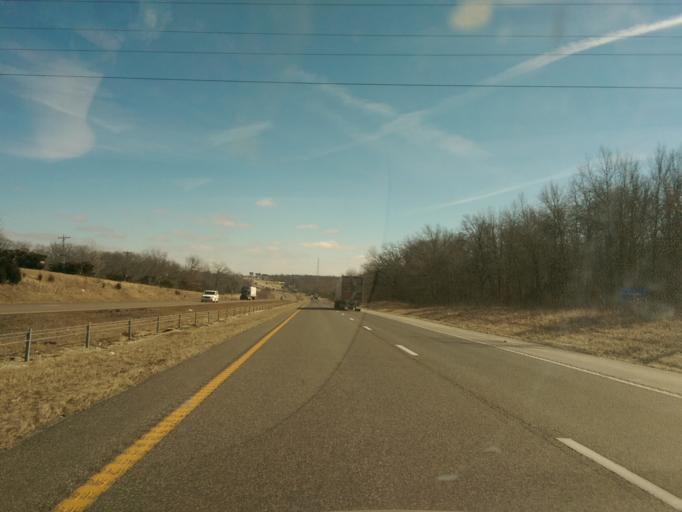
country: US
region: Missouri
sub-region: Boone County
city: Hallsville
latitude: 38.9559
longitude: -92.1612
